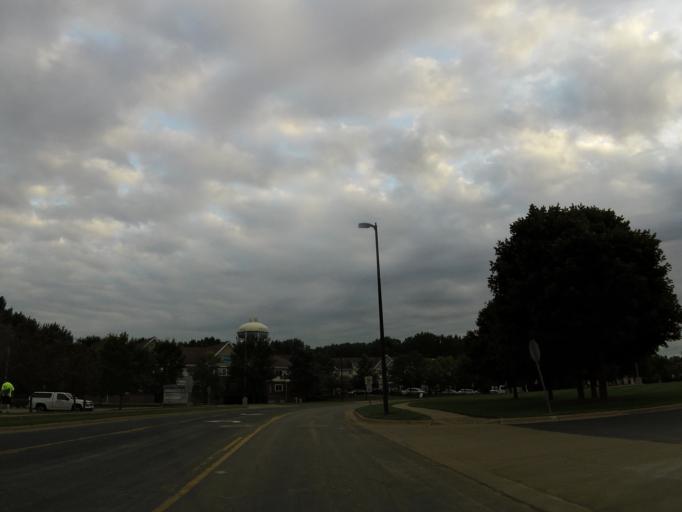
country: US
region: Minnesota
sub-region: Scott County
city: Prior Lake
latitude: 44.7079
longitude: -93.4249
